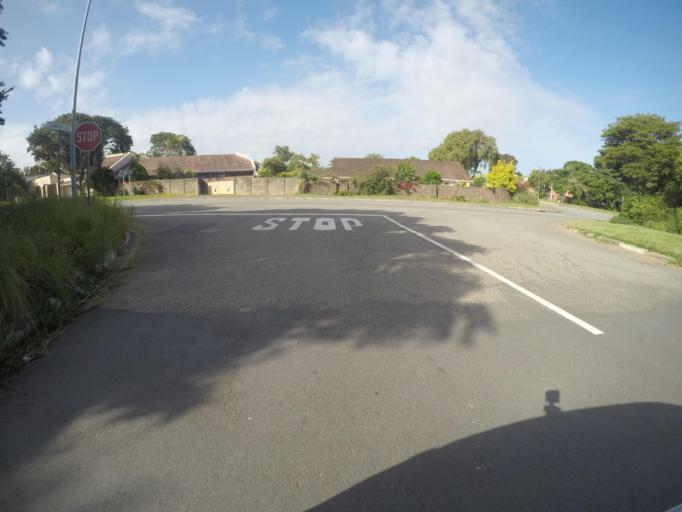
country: ZA
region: Eastern Cape
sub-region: Buffalo City Metropolitan Municipality
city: East London
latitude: -32.9725
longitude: 27.9552
